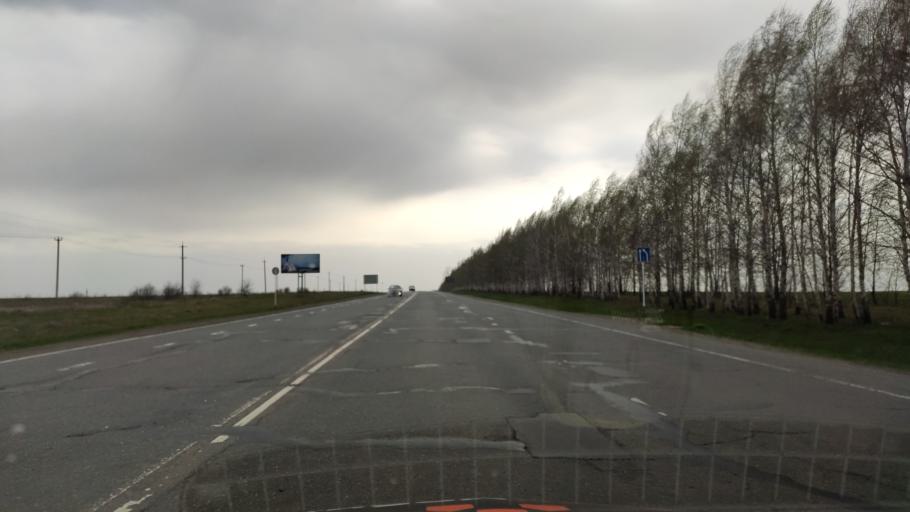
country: RU
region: Kursk
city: Gorshechnoye
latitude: 51.5068
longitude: 37.9953
